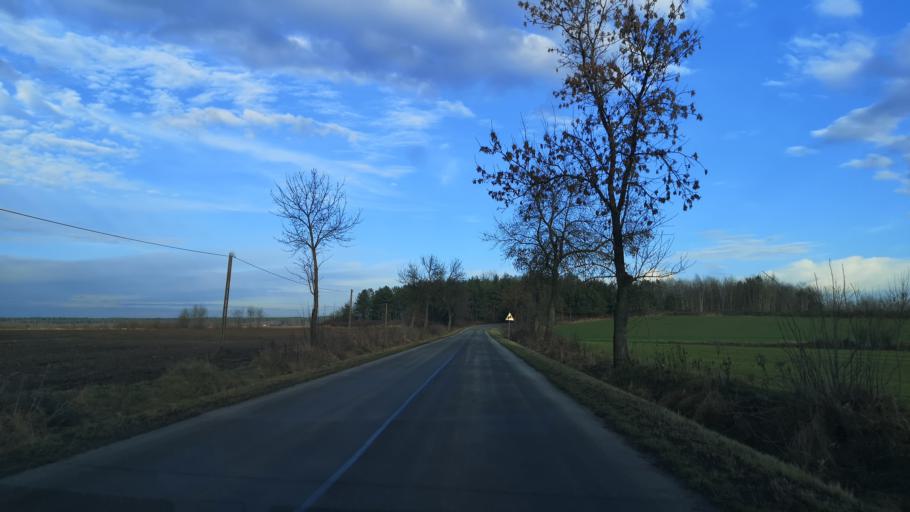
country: PL
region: Subcarpathian Voivodeship
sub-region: Powiat lezajski
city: Piskorowice
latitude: 50.2412
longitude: 22.5369
